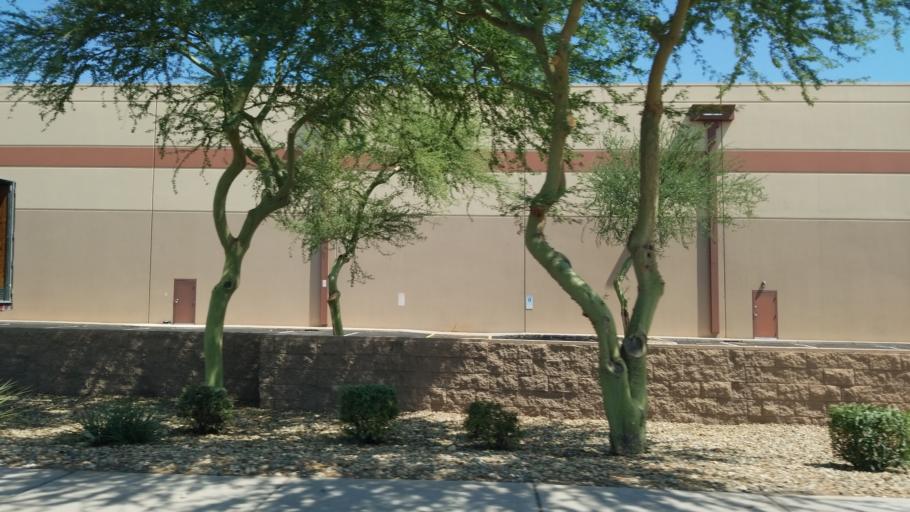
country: US
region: Arizona
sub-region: Maricopa County
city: Laveen
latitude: 33.4312
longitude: -112.1572
